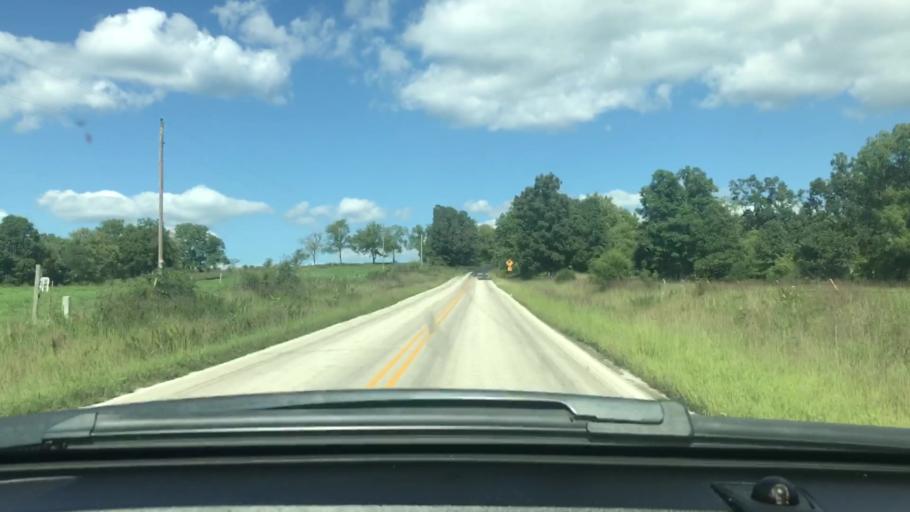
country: US
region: Missouri
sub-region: Wright County
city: Hartville
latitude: 37.3753
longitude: -92.3831
